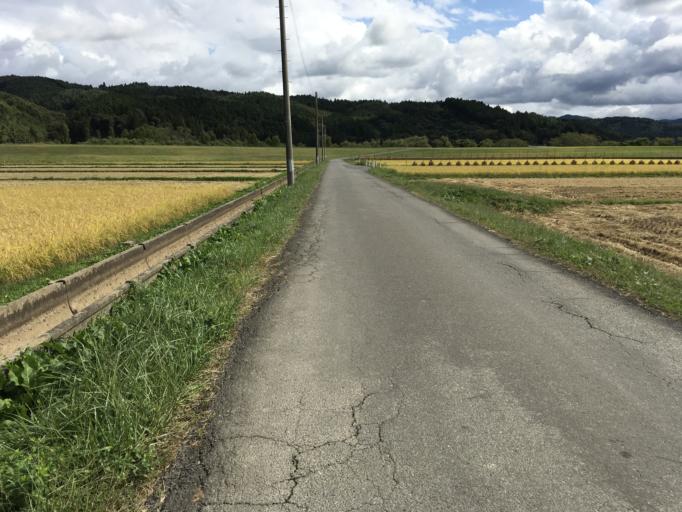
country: JP
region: Miyagi
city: Wakuya
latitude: 38.7285
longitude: 141.2902
